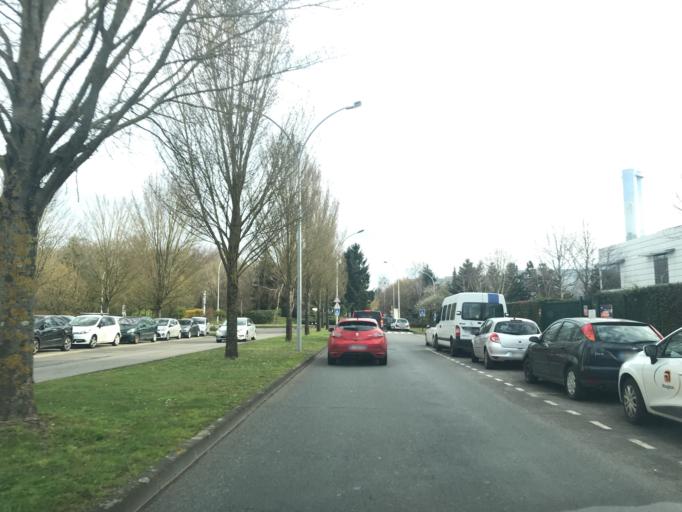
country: FR
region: Ile-de-France
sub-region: Departement des Yvelines
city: Velizy-Villacoublay
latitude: 48.7824
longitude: 2.2052
